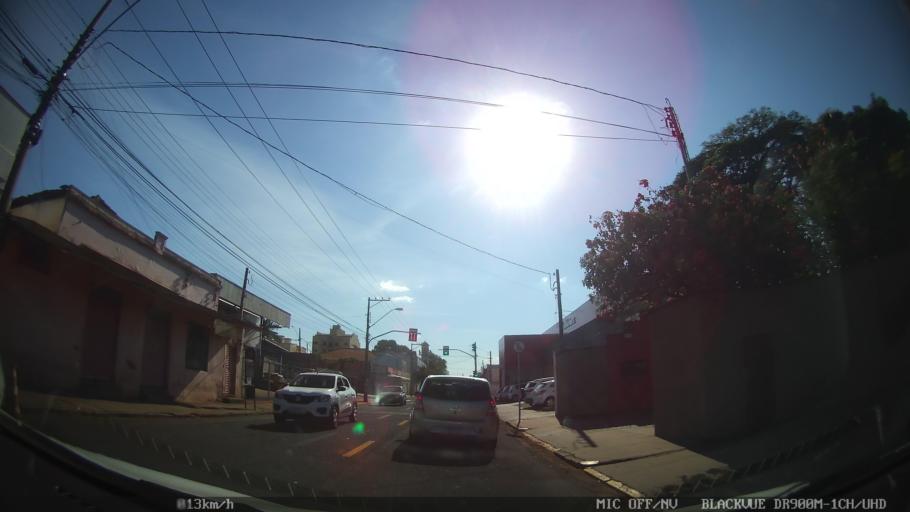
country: BR
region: Sao Paulo
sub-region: Ribeirao Preto
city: Ribeirao Preto
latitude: -21.1734
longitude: -47.7854
